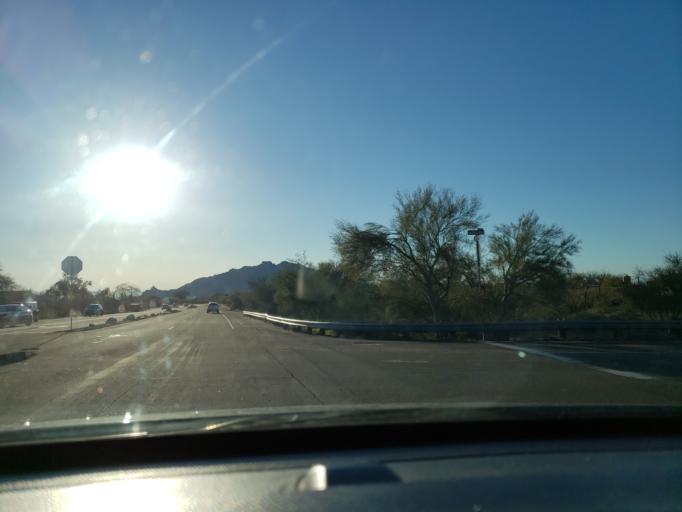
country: US
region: Arizona
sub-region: Maricopa County
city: Carefree
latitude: 33.8184
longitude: -111.8912
